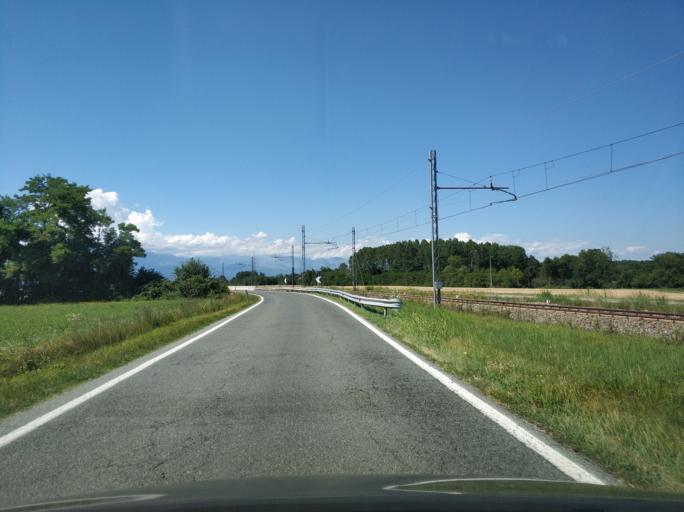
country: IT
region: Piedmont
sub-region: Provincia di Torino
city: San Benigno Canavese
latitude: 45.2413
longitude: 7.7731
